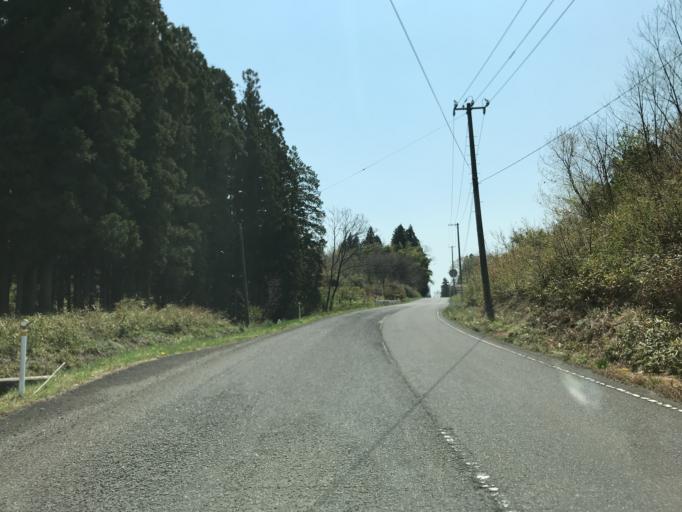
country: JP
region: Fukushima
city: Ishikawa
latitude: 37.1013
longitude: 140.4056
